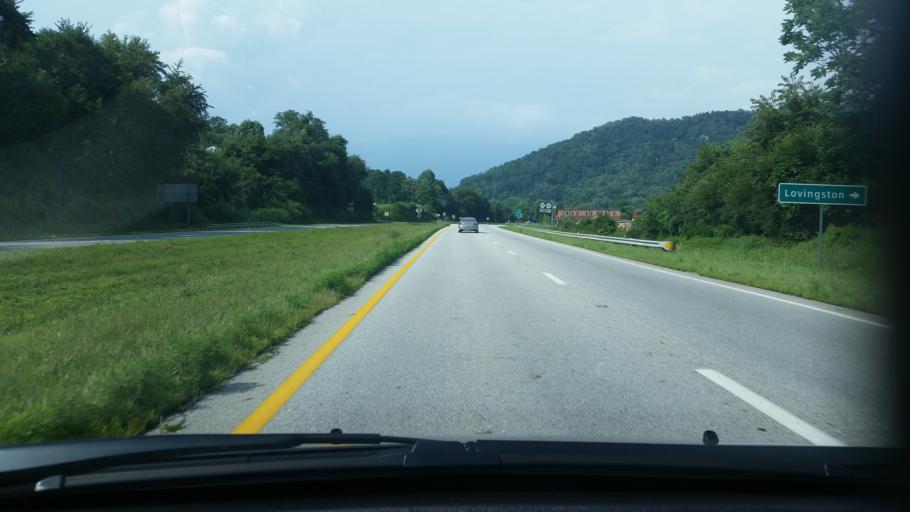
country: US
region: Virginia
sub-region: Nelson County
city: Lovingston
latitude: 37.7585
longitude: -78.8742
